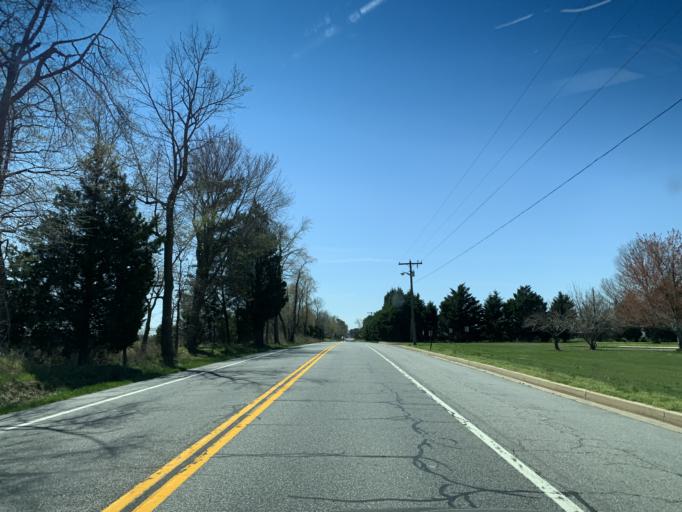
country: US
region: Maryland
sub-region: Talbot County
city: Easton
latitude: 38.8624
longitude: -76.0069
